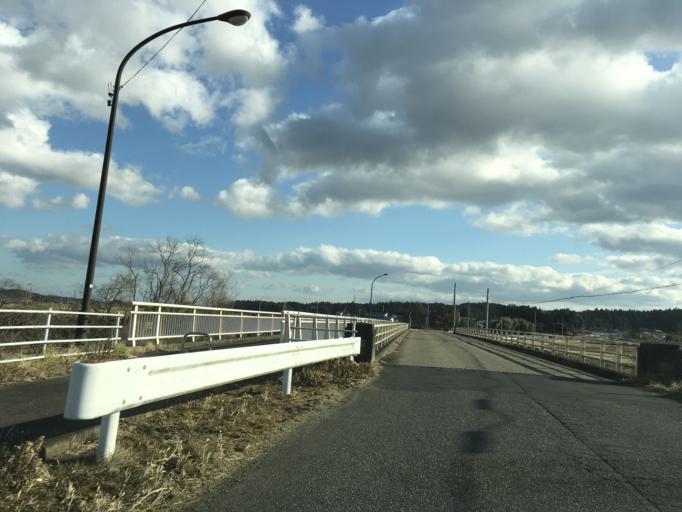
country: JP
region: Iwate
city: Ichinoseki
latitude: 38.8255
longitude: 141.0000
